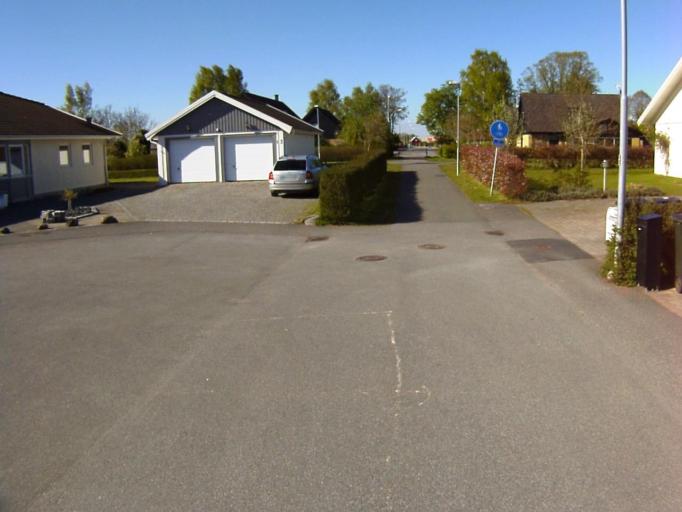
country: SE
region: Skane
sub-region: Kristianstads Kommun
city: Kristianstad
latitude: 56.0304
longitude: 14.2063
